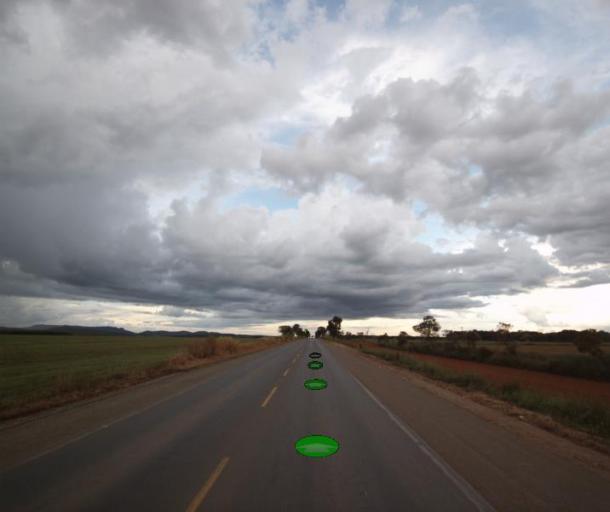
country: BR
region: Goias
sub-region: Uruacu
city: Uruacu
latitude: -14.7698
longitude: -49.2654
